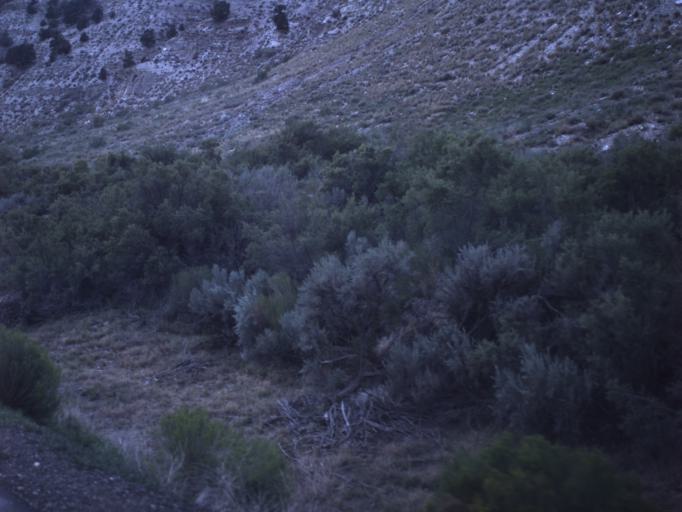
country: US
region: Utah
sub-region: Duchesne County
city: Duchesne
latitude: 40.0774
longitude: -110.5076
